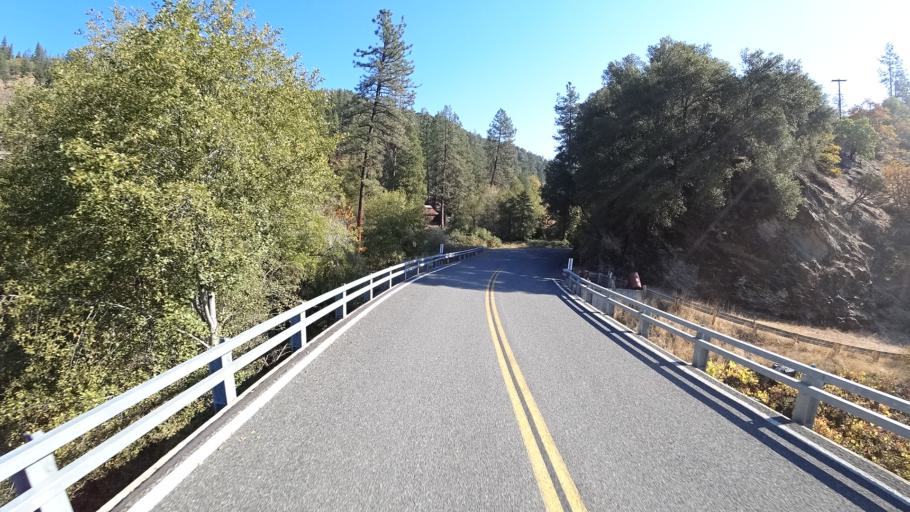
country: US
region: California
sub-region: Siskiyou County
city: Yreka
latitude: 41.7430
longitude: -123.0030
